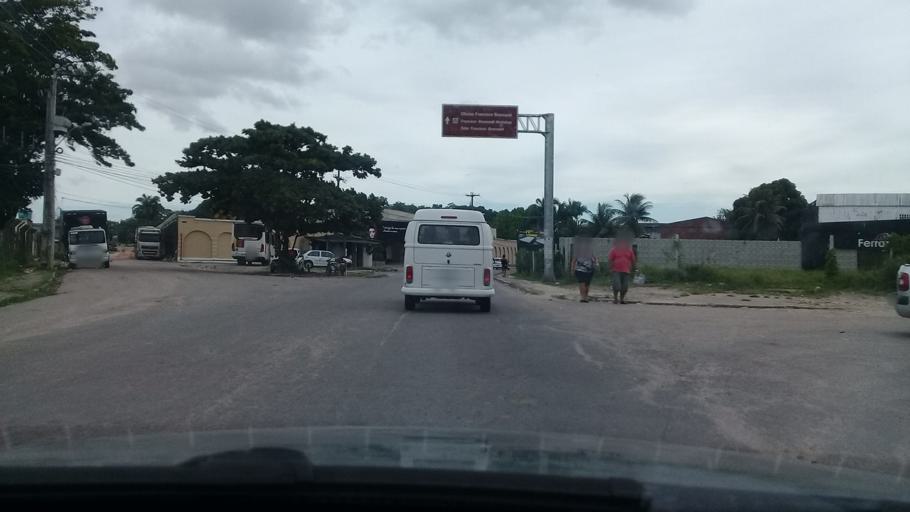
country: BR
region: Pernambuco
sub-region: Sao Lourenco Da Mata
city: Sao Lourenco da Mata
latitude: -8.0308
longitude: -34.9584
